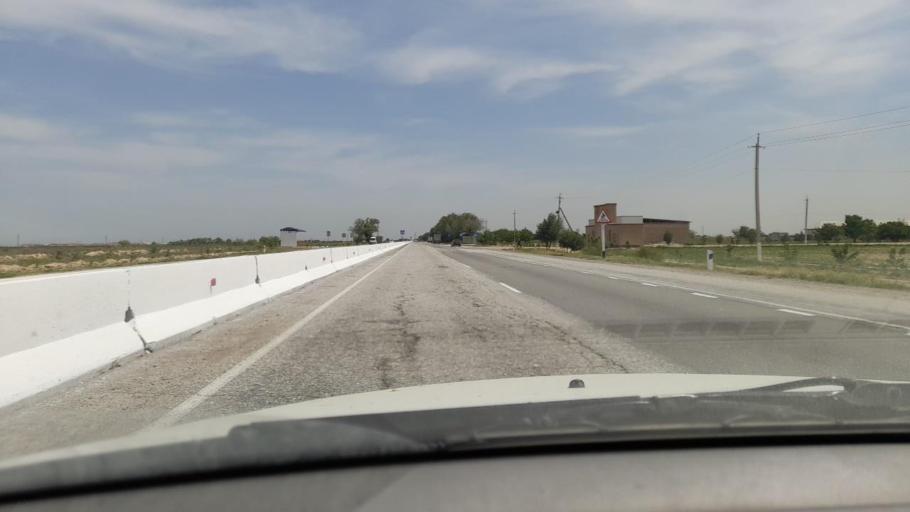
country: UZ
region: Navoiy
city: Konimex
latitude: 40.1103
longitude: 65.0638
